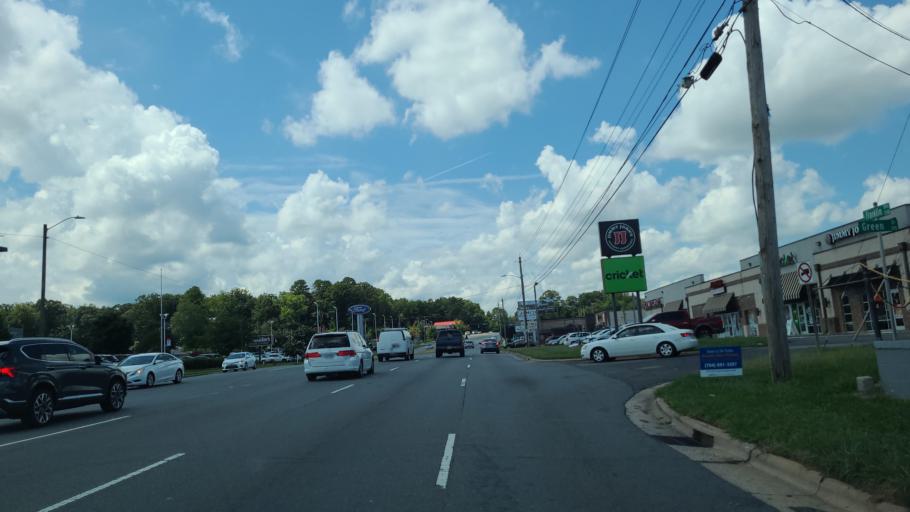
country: US
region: North Carolina
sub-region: Gaston County
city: Ranlo
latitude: 35.2616
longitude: -81.1418
